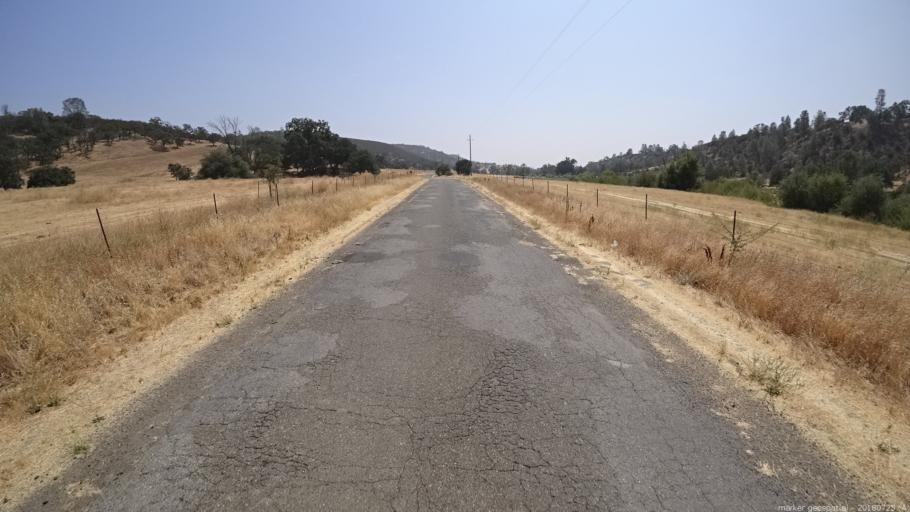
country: US
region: California
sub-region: Fresno County
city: Coalinga
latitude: 35.9450
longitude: -120.4677
